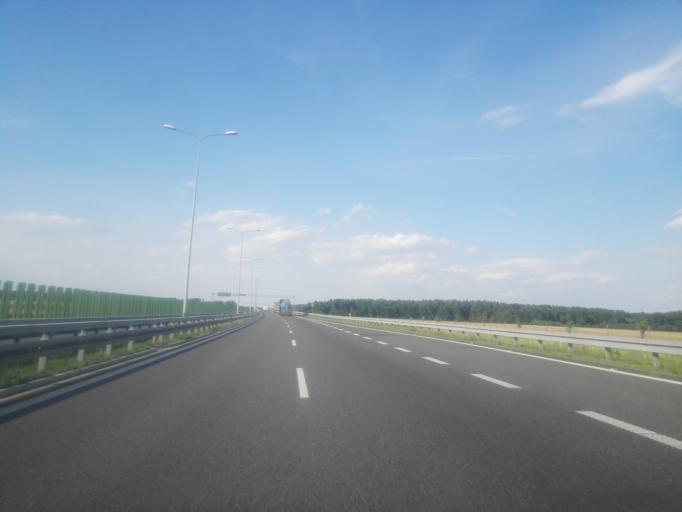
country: PL
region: Lower Silesian Voivodeship
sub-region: Powiat olesnicki
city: Twardogora
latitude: 51.2862
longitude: 17.5752
